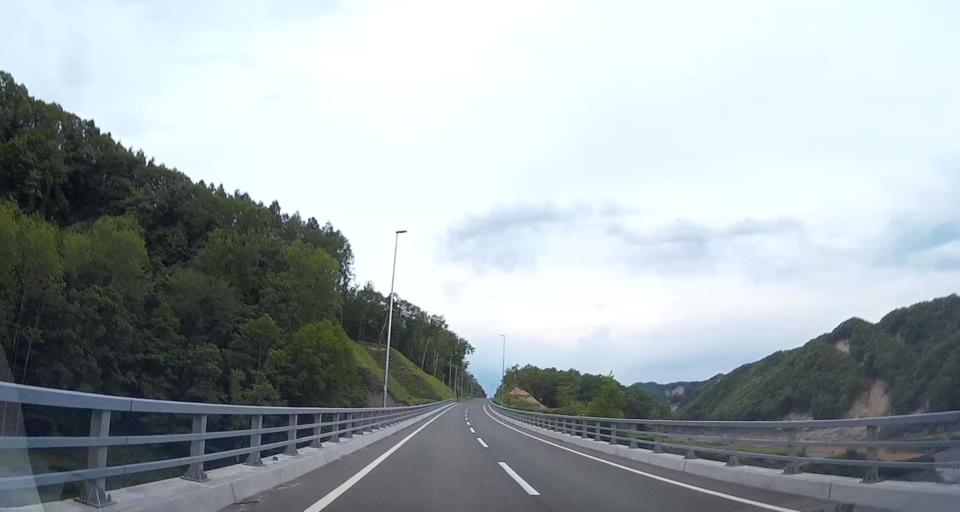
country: JP
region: Hokkaido
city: Chitose
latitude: 42.7836
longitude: 142.0214
